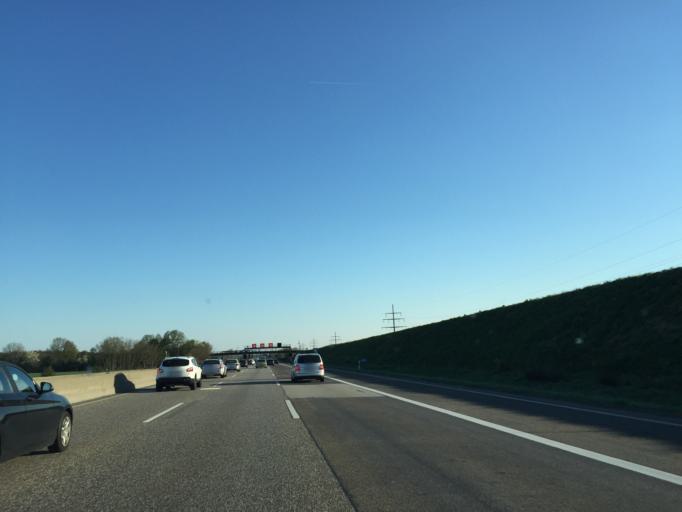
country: DE
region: Hesse
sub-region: Regierungsbezirk Darmstadt
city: Friedrichsdorf
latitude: 50.2450
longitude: 8.6628
